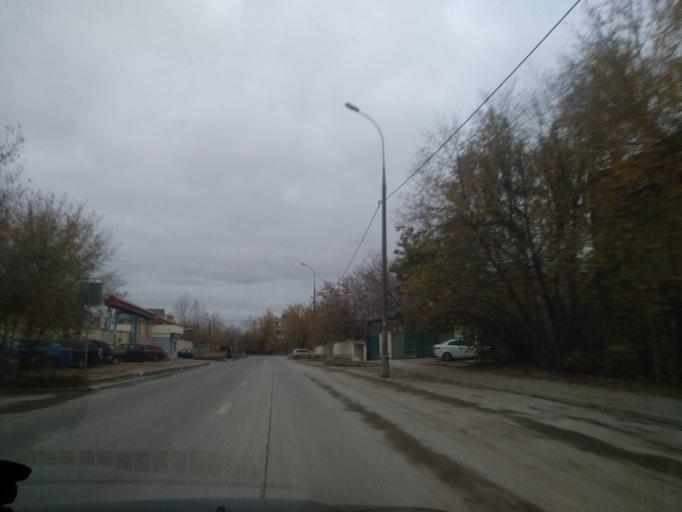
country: RU
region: Moscow
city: Kozeyevo
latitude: 55.8836
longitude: 37.6304
